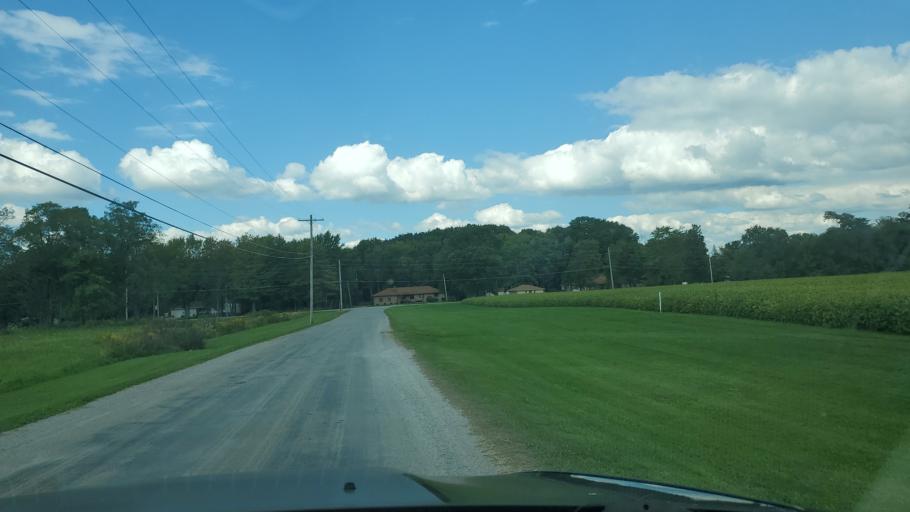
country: US
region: Ohio
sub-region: Mahoning County
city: New Middletown
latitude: 40.9862
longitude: -80.5902
